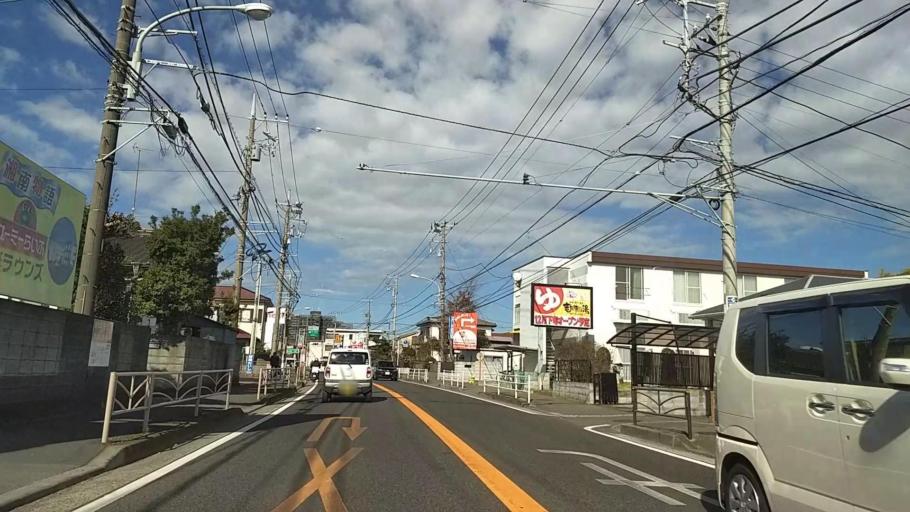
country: JP
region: Kanagawa
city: Chigasaki
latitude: 35.3313
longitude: 139.3886
